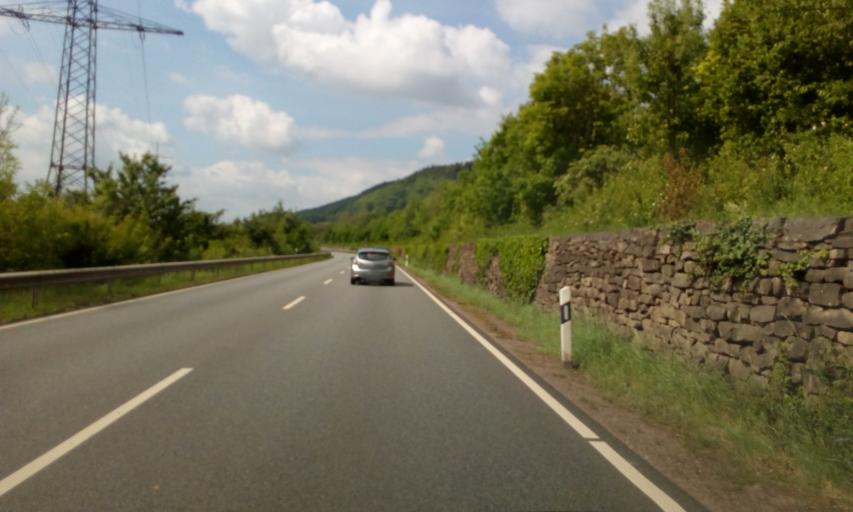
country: DE
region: Rheinland-Pfalz
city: Kenn
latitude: 49.8082
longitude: 6.6928
